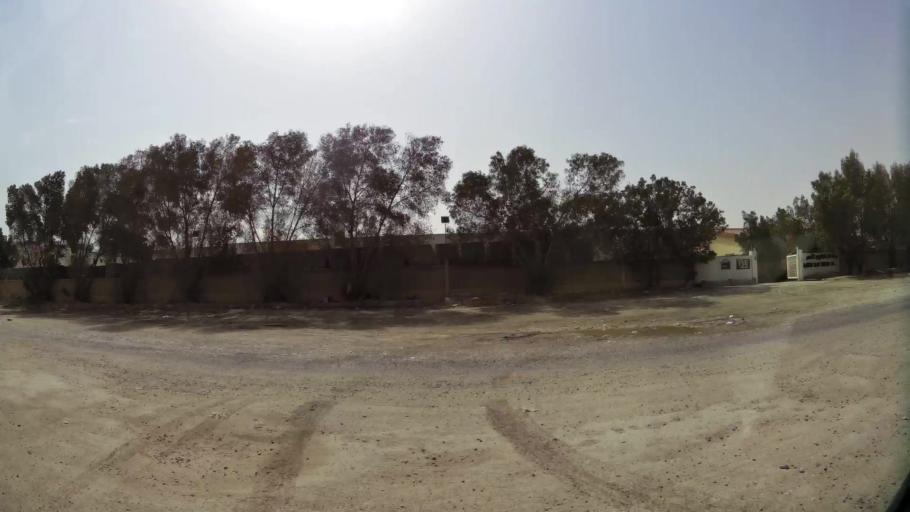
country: QA
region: Al Wakrah
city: Al Wukayr
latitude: 25.1682
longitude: 51.4613
